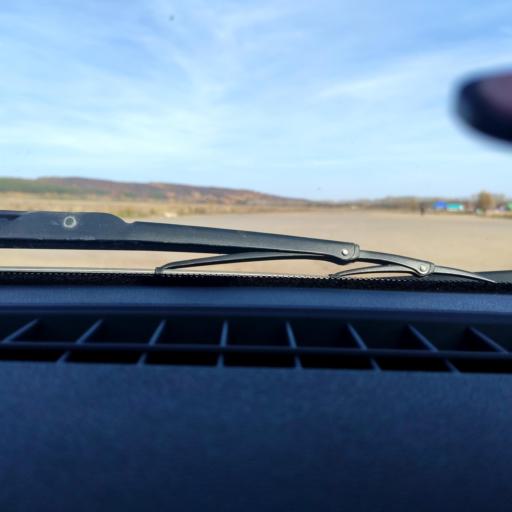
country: RU
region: Bashkortostan
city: Ufa
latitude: 54.8357
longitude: 56.1710
